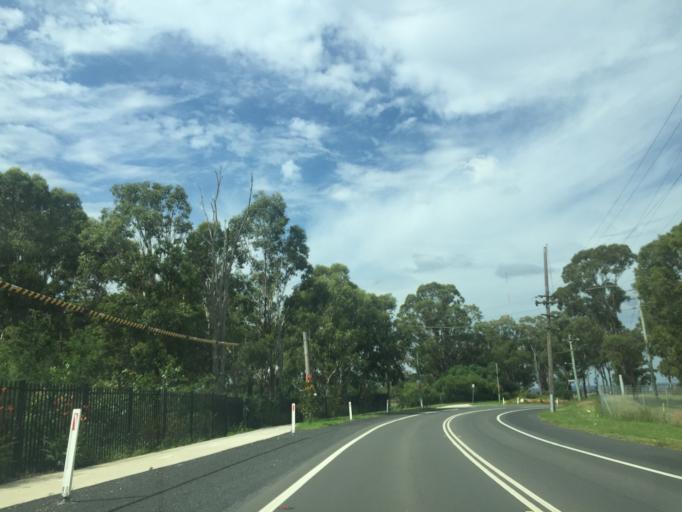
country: AU
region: New South Wales
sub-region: Holroyd
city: Girraween
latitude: -33.8094
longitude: 150.9129
